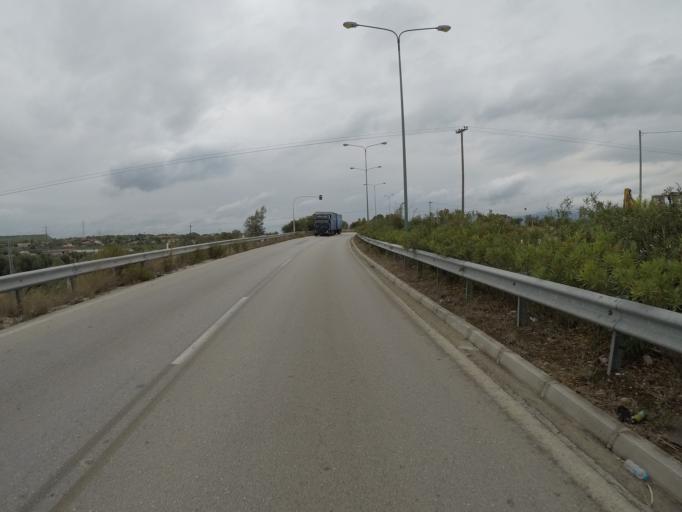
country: GR
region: Peloponnese
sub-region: Nomos Korinthias
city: Kyras Vrysi
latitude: 37.9311
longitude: 22.9933
